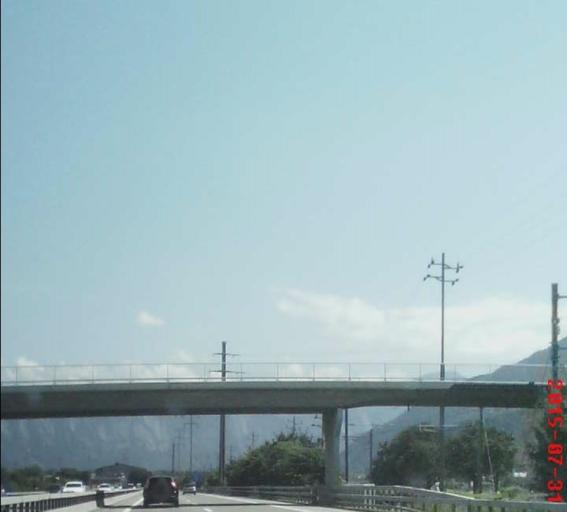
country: CH
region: Saint Gallen
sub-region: Wahlkreis Sarganserland
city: Bad Ragaz
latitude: 47.0218
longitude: 9.4845
